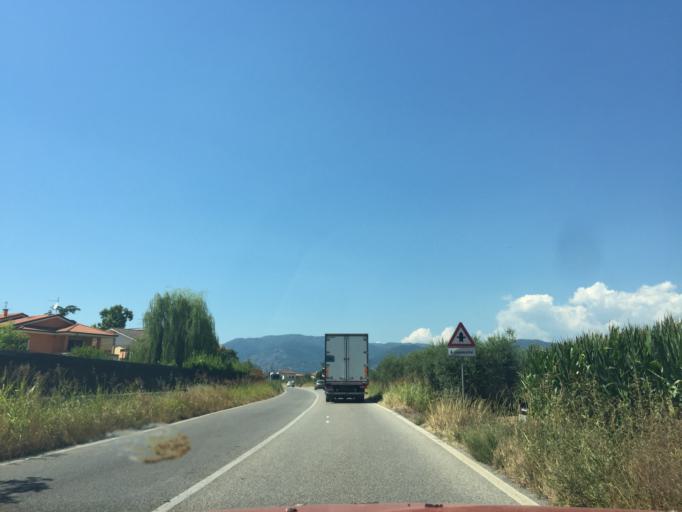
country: IT
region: Tuscany
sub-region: Provincia di Pistoia
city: Chiesina Uzzanese
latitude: 43.8521
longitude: 10.7084
